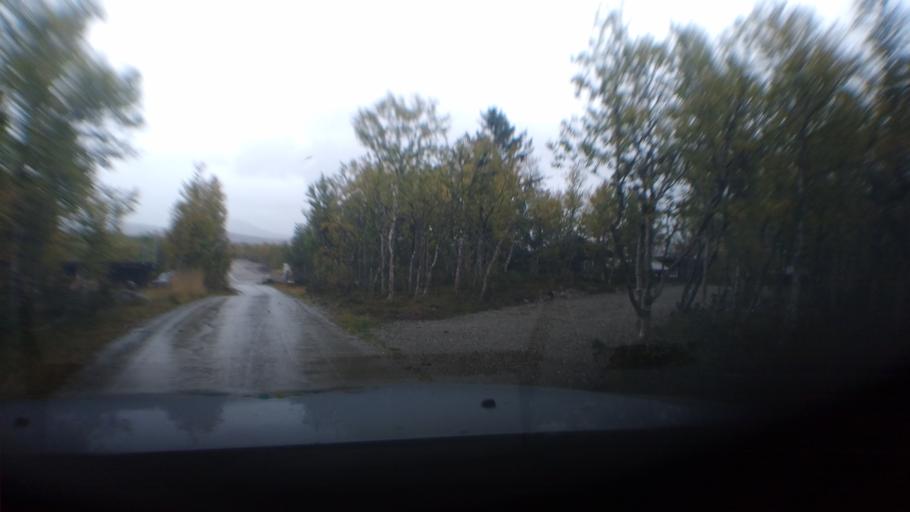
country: NO
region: Oppland
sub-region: Ringebu
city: Ringebu
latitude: 61.6531
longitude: 10.1013
